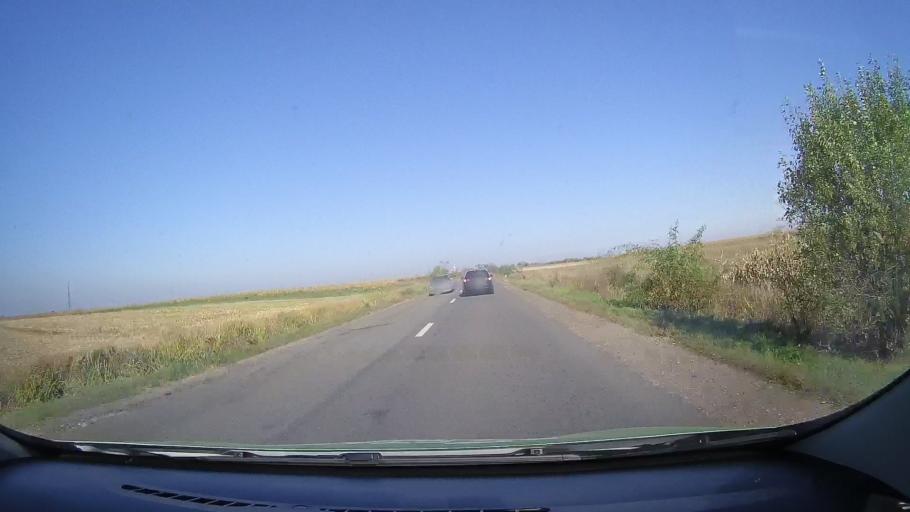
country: RO
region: Satu Mare
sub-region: Comuna Cauas
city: Cauas
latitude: 47.6143
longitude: 22.5372
